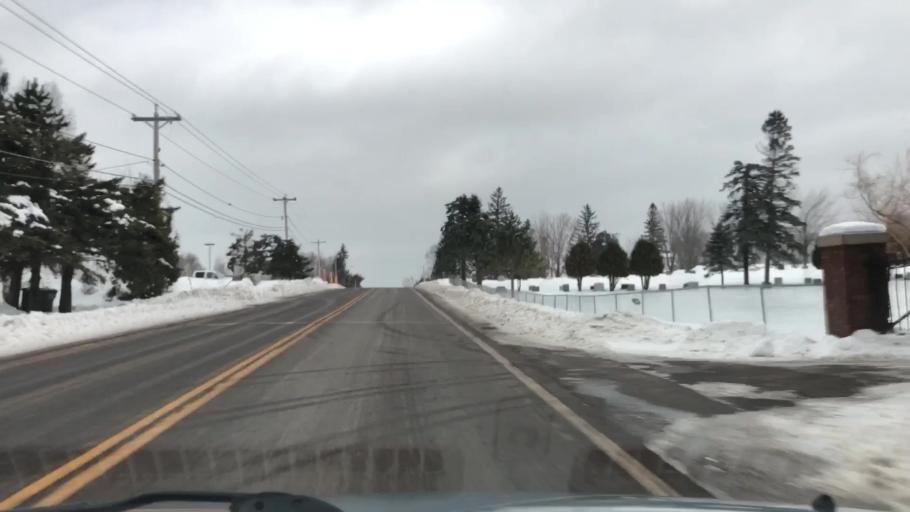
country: US
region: Minnesota
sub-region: Saint Louis County
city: Arnold
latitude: 46.8603
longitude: -92.1111
